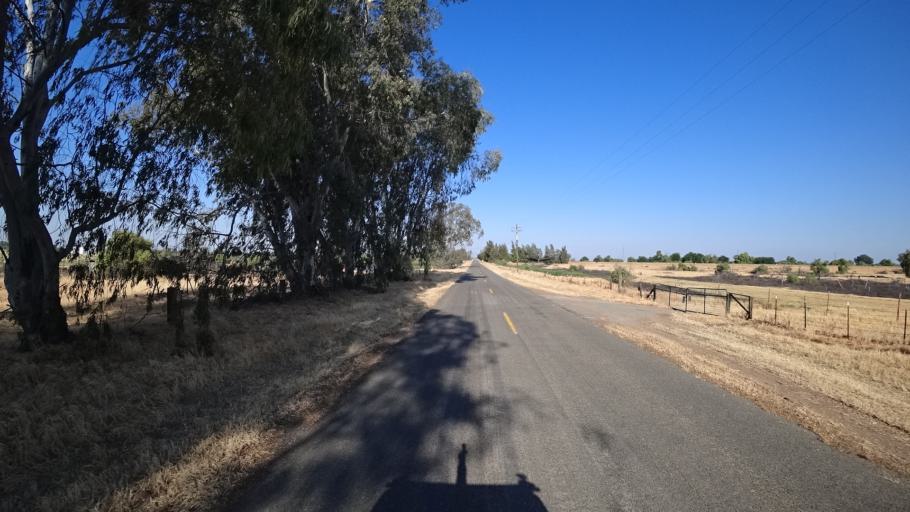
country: US
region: California
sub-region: Fresno County
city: Riverdale
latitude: 36.3766
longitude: -119.8796
